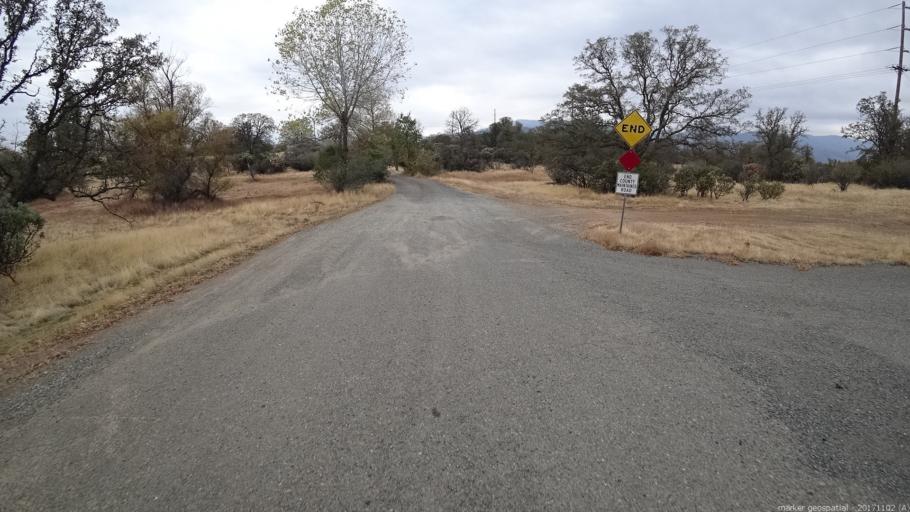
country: US
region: California
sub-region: Shasta County
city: Shasta
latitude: 40.6311
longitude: -122.4379
